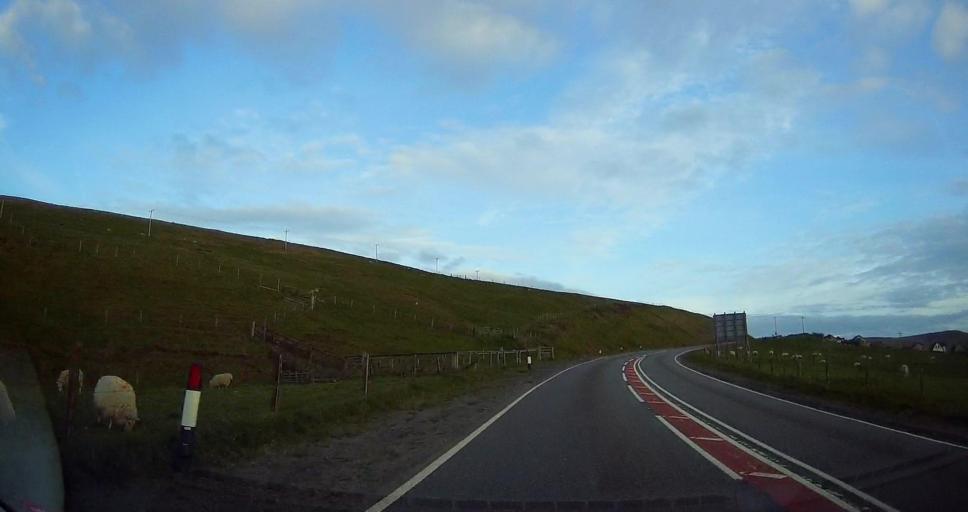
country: GB
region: Scotland
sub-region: Shetland Islands
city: Lerwick
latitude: 60.1857
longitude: -1.2254
